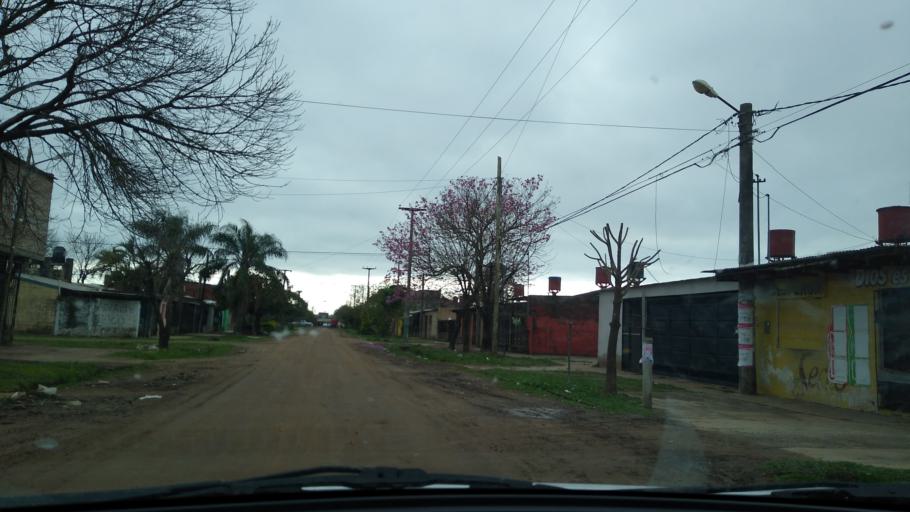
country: AR
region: Chaco
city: Resistencia
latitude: -27.4883
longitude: -58.9779
